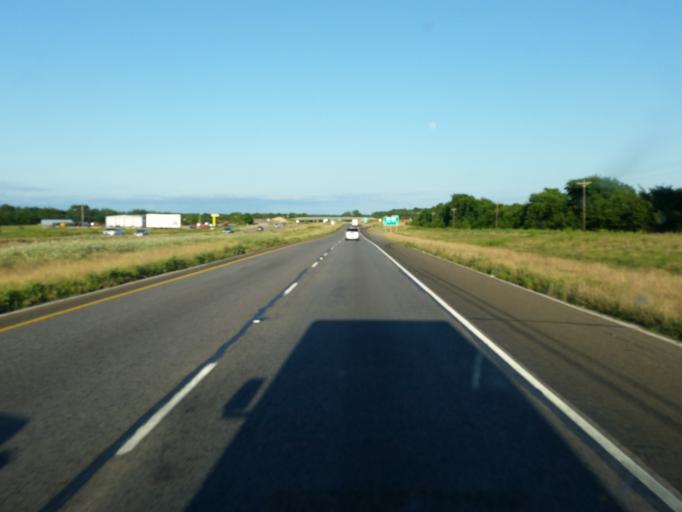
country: US
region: Texas
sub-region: Kaufman County
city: Terrell
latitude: 32.6832
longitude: -96.2042
